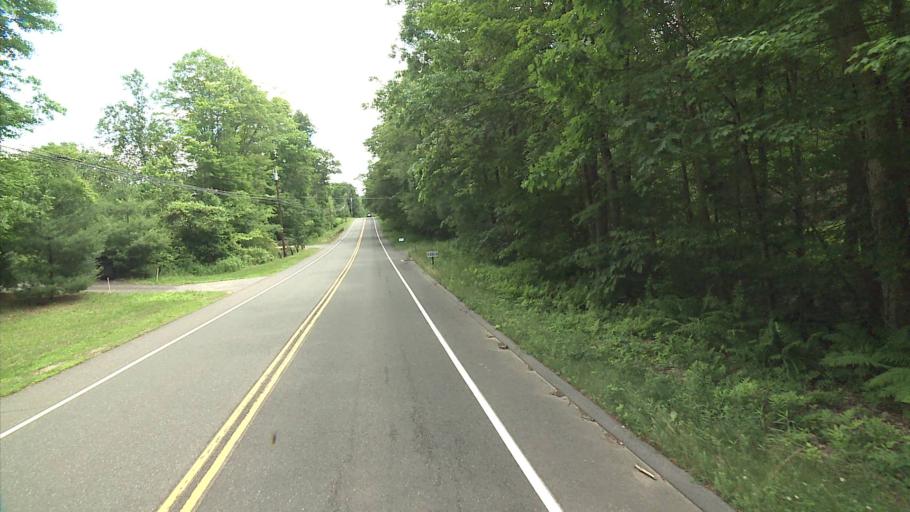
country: US
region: Connecticut
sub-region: Litchfield County
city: Bethlehem Village
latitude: 41.6710
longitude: -73.1700
